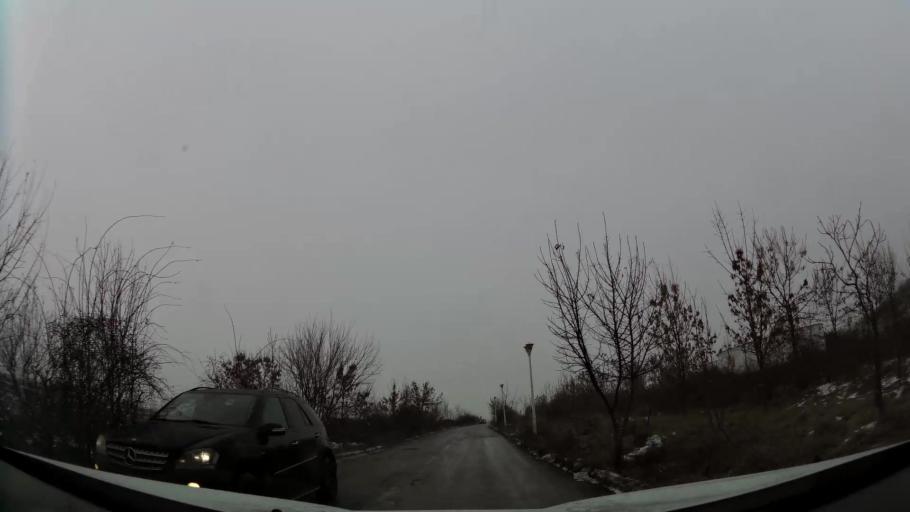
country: RO
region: Prahova
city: Ploiesti
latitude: 44.9639
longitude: 26.0038
